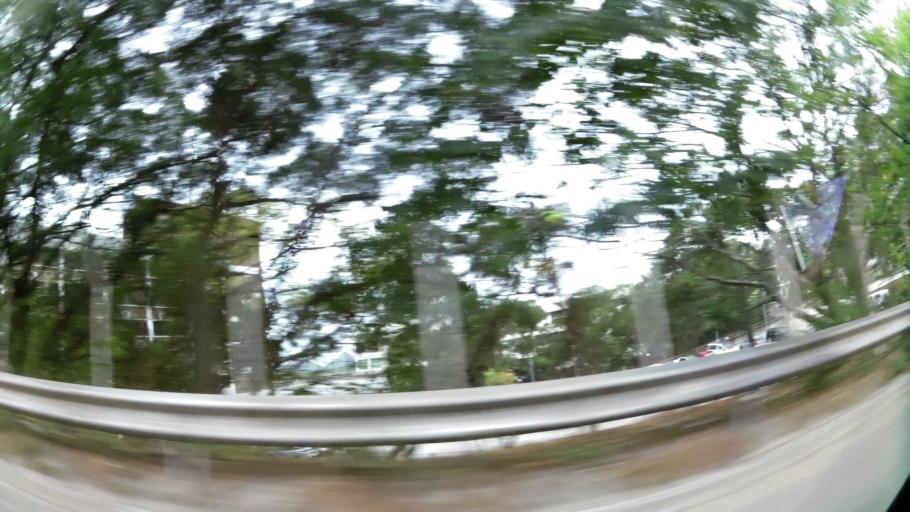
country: HK
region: Tsuen Wan
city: Tsuen Wan
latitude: 22.3400
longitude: 114.0939
